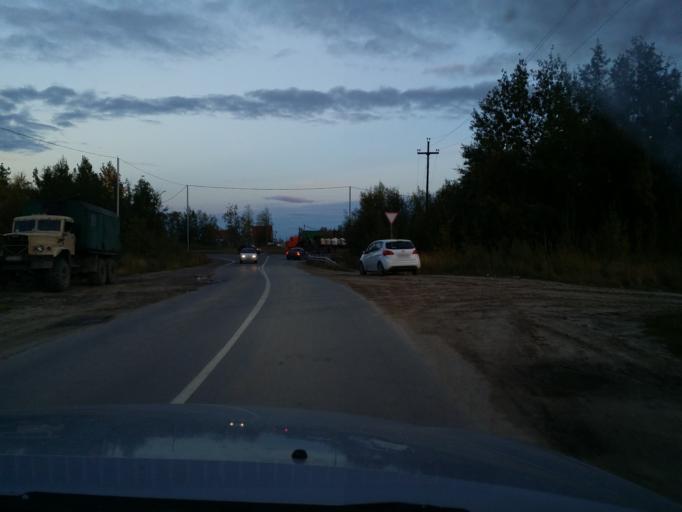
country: RU
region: Khanty-Mansiyskiy Avtonomnyy Okrug
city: Megion
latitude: 61.0644
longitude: 76.1851
